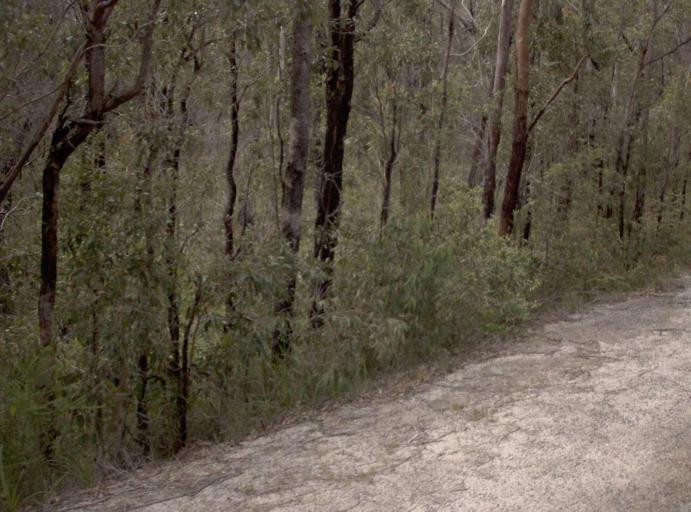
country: AU
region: New South Wales
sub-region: Bega Valley
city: Eden
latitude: -37.4029
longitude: 149.6675
